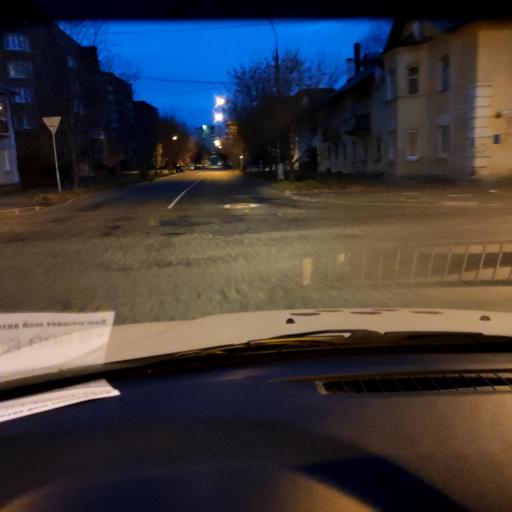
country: RU
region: Samara
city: Tol'yatti
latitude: 53.5042
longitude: 49.3937
